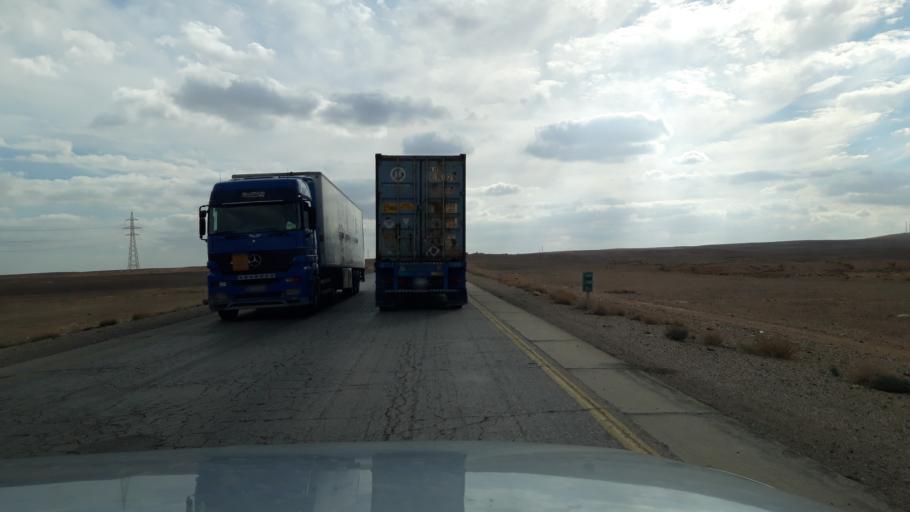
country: JO
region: Amman
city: Al Azraq ash Shamali
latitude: 31.7585
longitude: 36.5505
